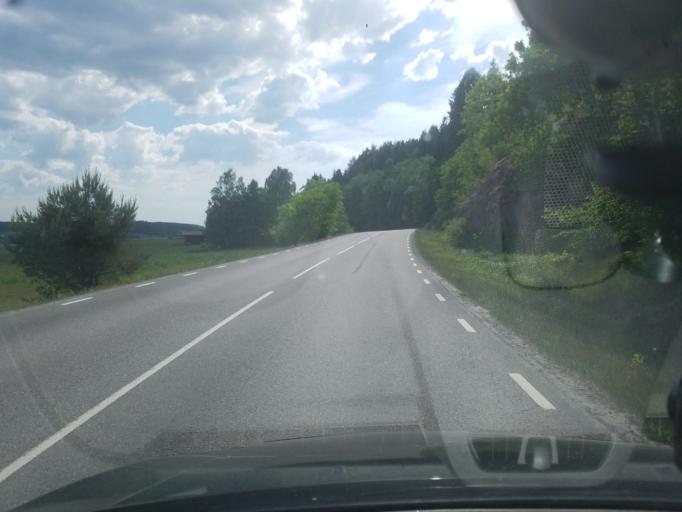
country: SE
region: Vaestra Goetaland
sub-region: Ale Kommun
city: Alvangen
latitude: 57.9663
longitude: 12.1036
